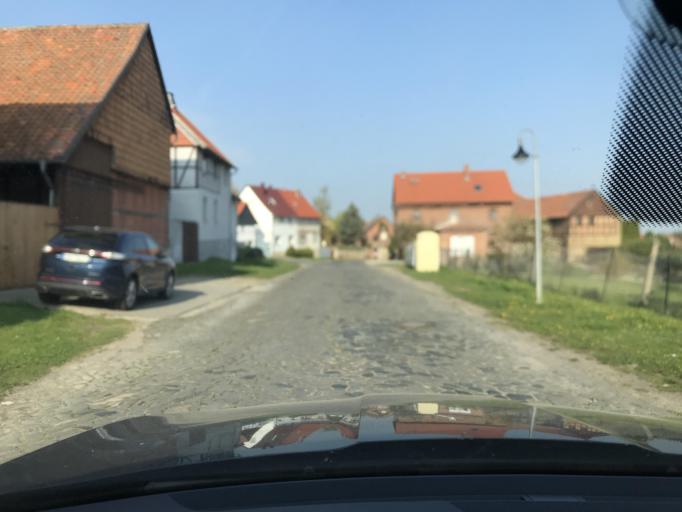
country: DE
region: Saxony-Anhalt
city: Huy-Neinstedt
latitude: 51.9738
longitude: 10.9845
